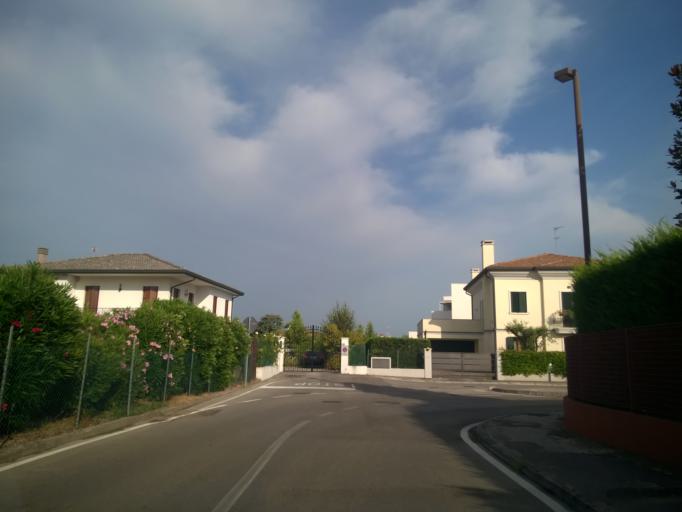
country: IT
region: Veneto
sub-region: Provincia di Padova
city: Piove di Sacco-Piovega
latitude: 45.2894
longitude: 12.0352
